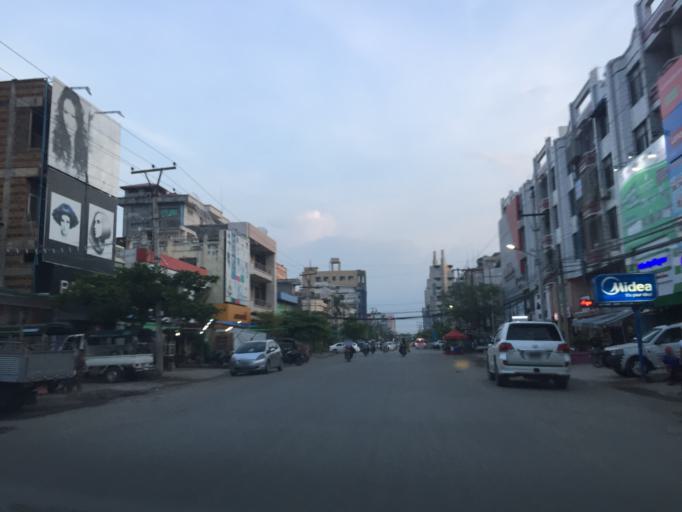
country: MM
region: Mandalay
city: Mandalay
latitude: 21.9745
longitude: 96.0884
